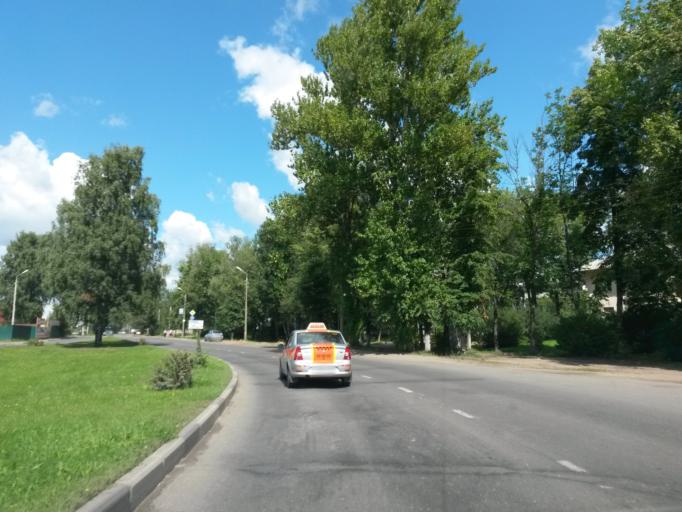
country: RU
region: Jaroslavl
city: Yaroslavl
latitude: 57.6468
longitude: 39.9100
